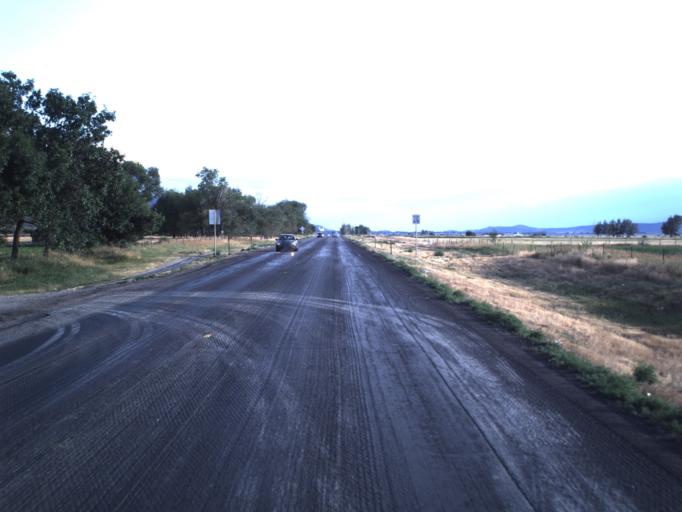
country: US
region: Utah
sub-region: Sanpete County
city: Ephraim
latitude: 39.3407
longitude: -111.5940
